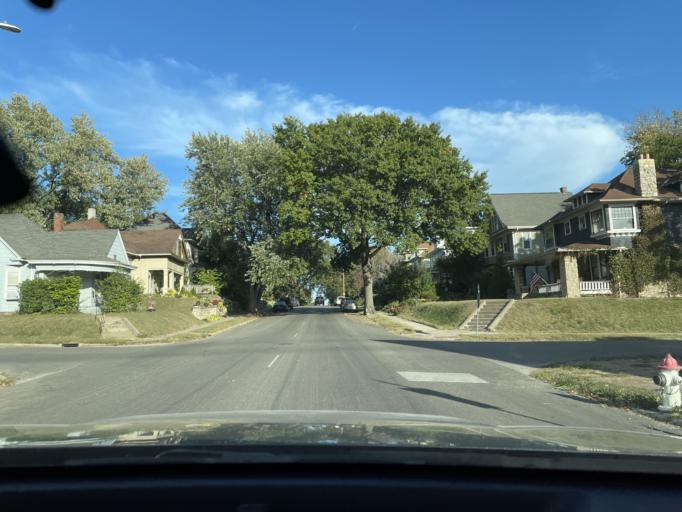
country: US
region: Missouri
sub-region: Buchanan County
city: Saint Joseph
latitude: 39.7683
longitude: -94.8306
